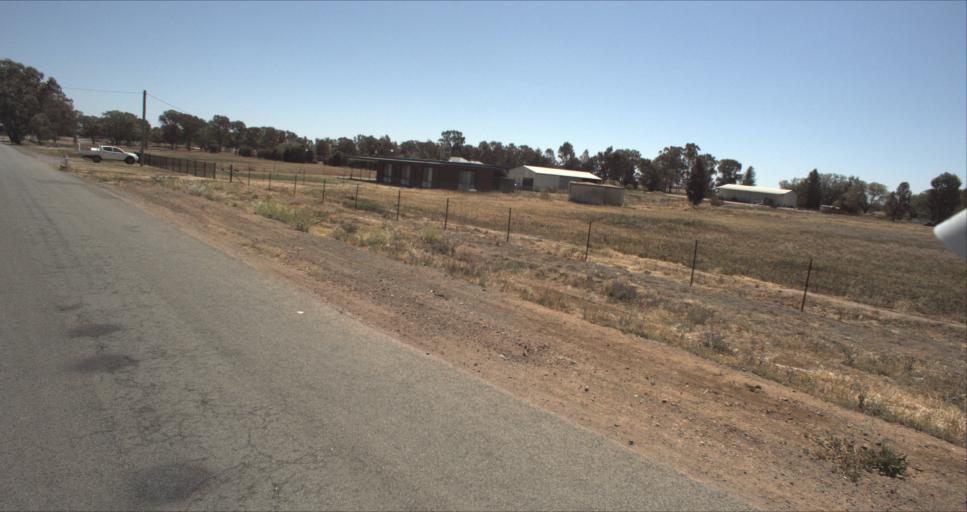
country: AU
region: New South Wales
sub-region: Leeton
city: Leeton
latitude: -34.5337
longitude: 146.4023
